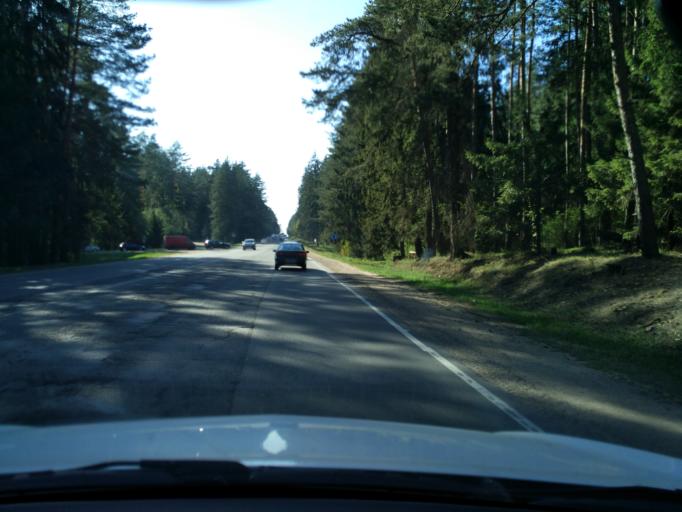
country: BY
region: Minsk
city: Borovlyany
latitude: 53.9613
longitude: 27.6907
